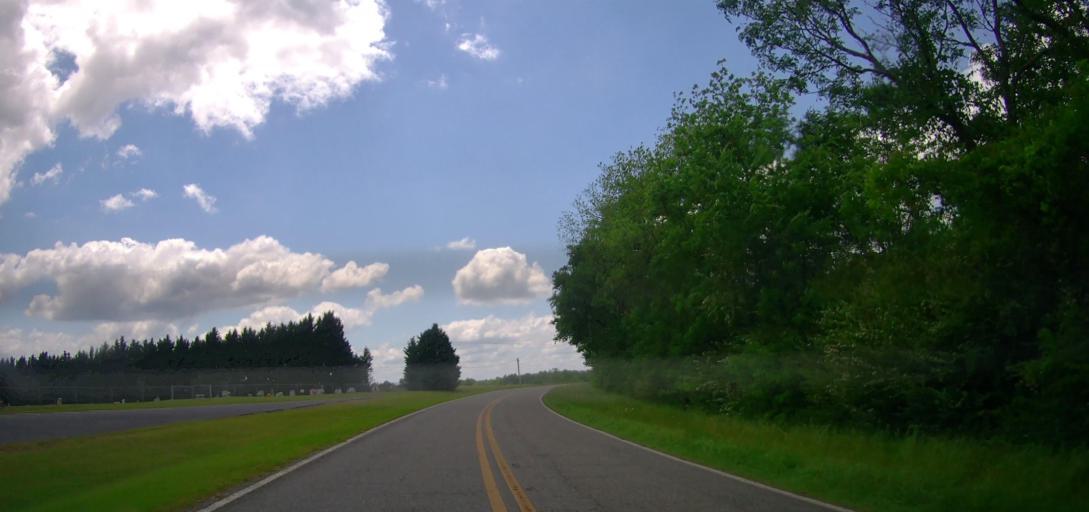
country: US
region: Georgia
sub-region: Laurens County
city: Dublin
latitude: 32.5977
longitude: -82.9267
